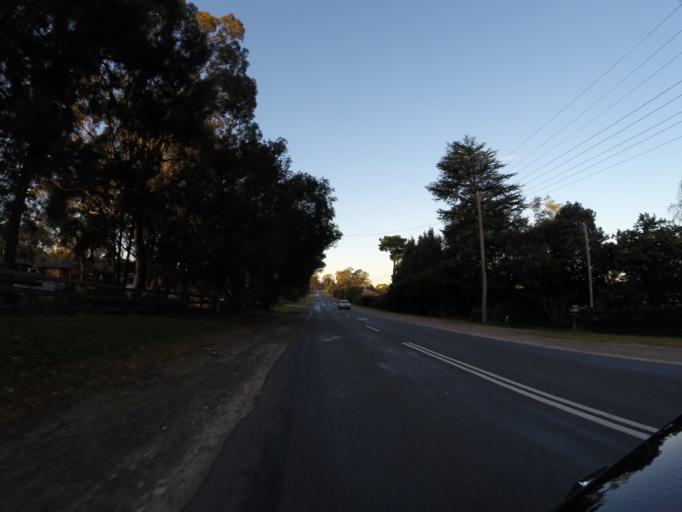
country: AU
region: New South Wales
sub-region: Camden
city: Cobbitty
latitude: -34.0194
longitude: 150.6714
